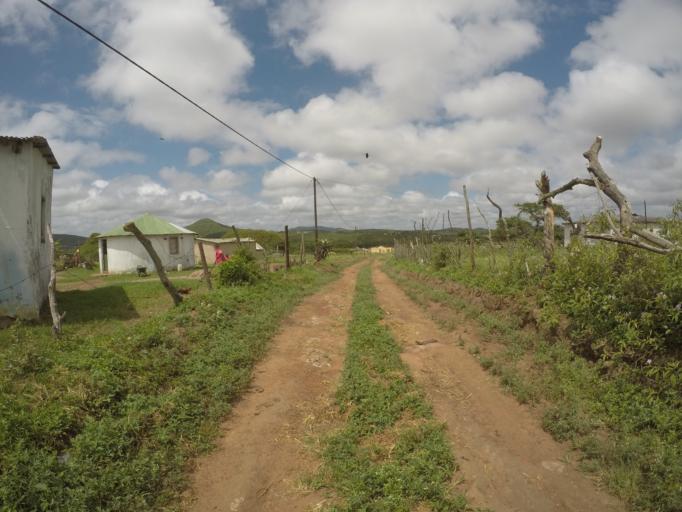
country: ZA
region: KwaZulu-Natal
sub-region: uThungulu District Municipality
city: Empangeni
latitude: -28.5825
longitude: 31.8495
